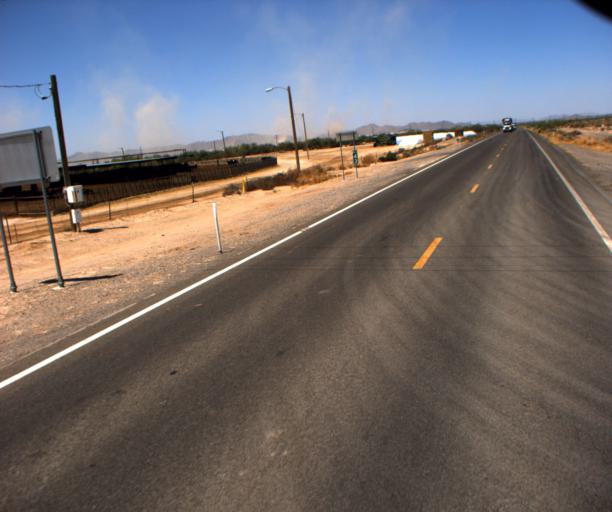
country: US
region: Arizona
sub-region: Pinal County
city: Maricopa
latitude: 33.0724
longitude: -112.0656
